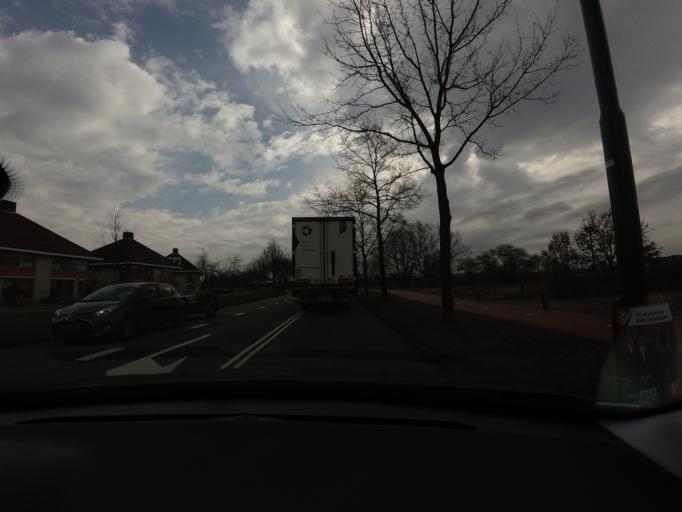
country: NL
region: North Brabant
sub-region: Gemeente Waalwijk
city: Waalwijk
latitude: 51.6516
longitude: 5.0259
